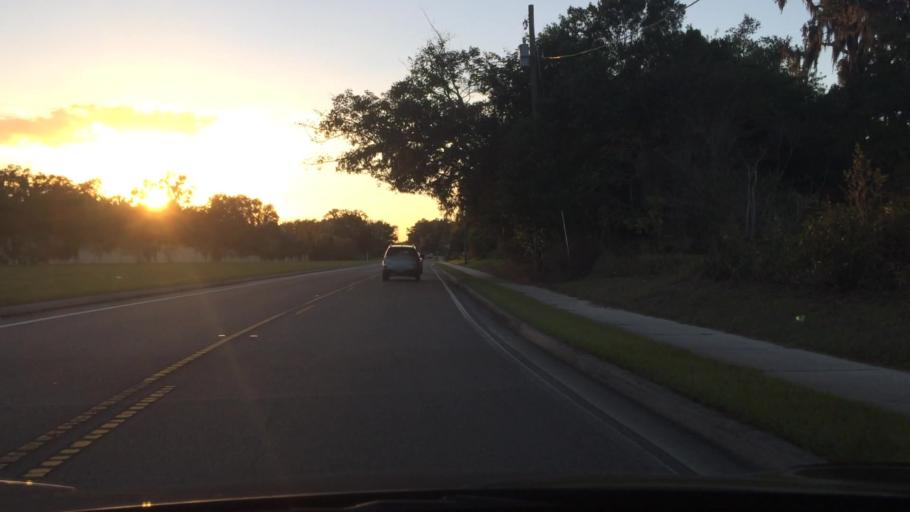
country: US
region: Florida
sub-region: Hillsborough County
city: Lutz
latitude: 28.1721
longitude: -82.4509
